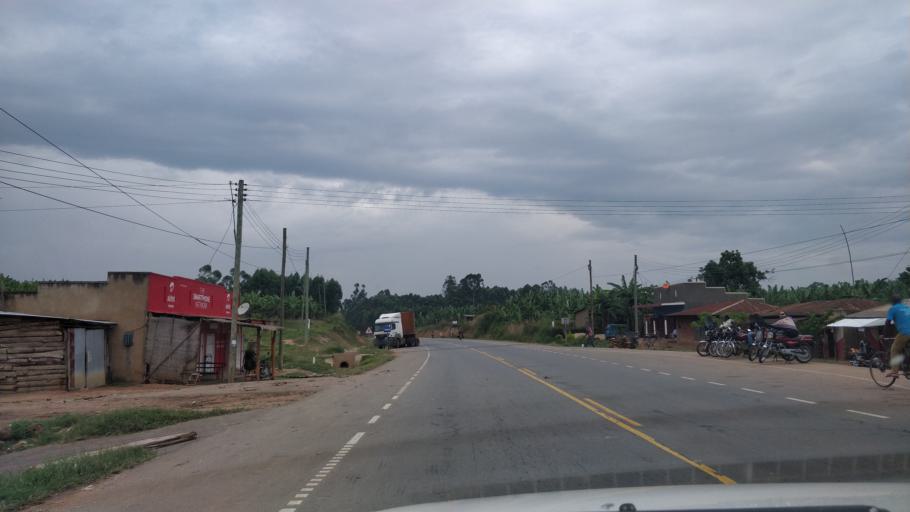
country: UG
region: Western Region
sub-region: Sheema District
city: Kibingo
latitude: -0.6679
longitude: 30.4438
